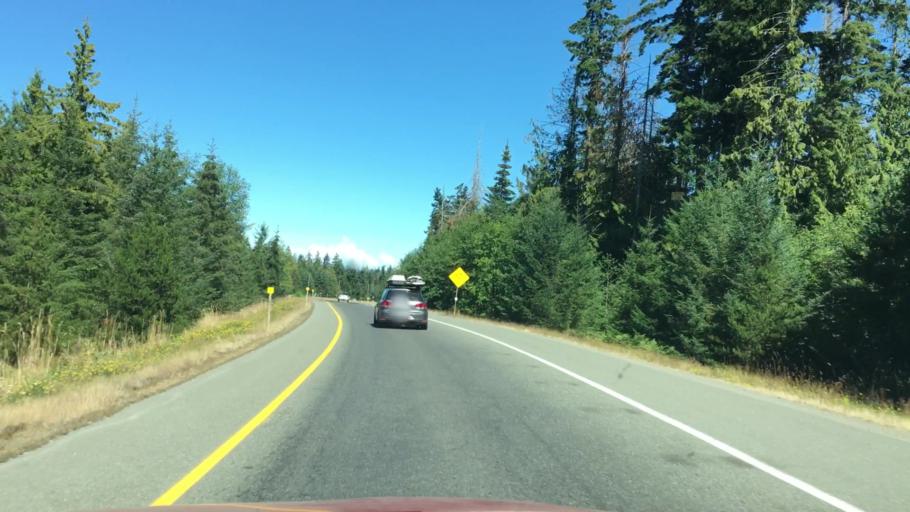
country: CA
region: British Columbia
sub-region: Regional District of Nanaimo
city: Parksville
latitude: 49.3239
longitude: -124.4386
